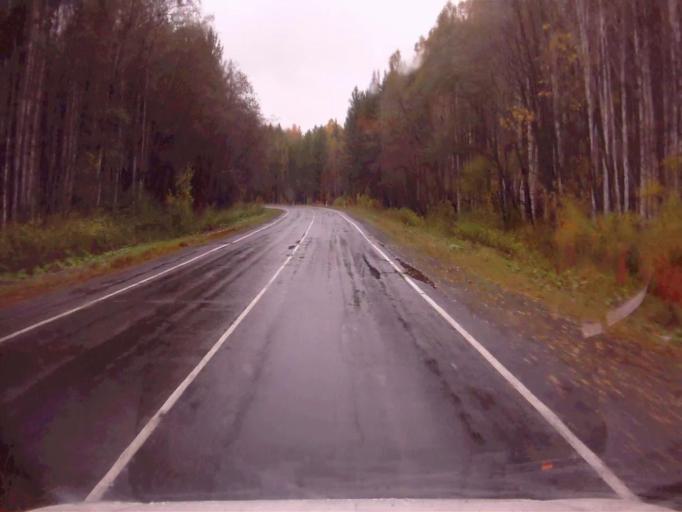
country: RU
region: Chelyabinsk
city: Verkhniy Ufaley
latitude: 55.9569
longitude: 60.3904
